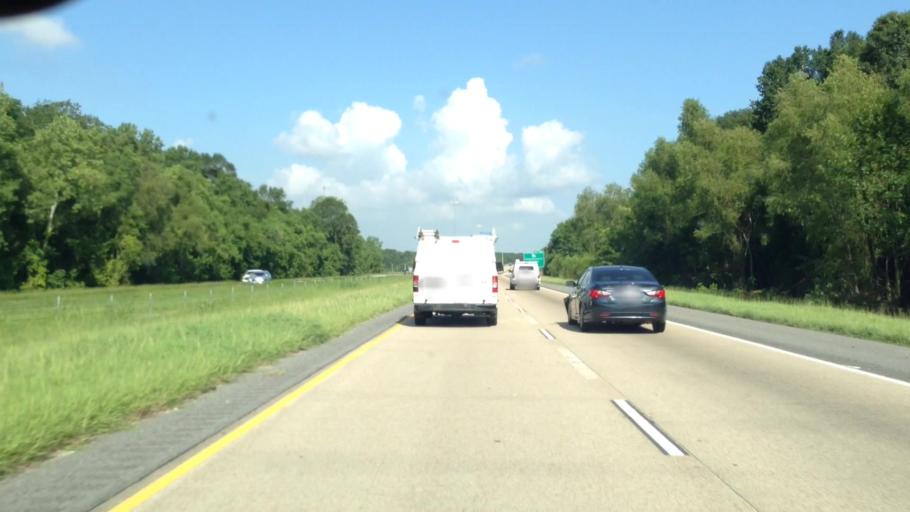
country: US
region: Louisiana
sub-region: Ascension Parish
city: Sorrento
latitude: 30.1690
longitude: -90.8675
